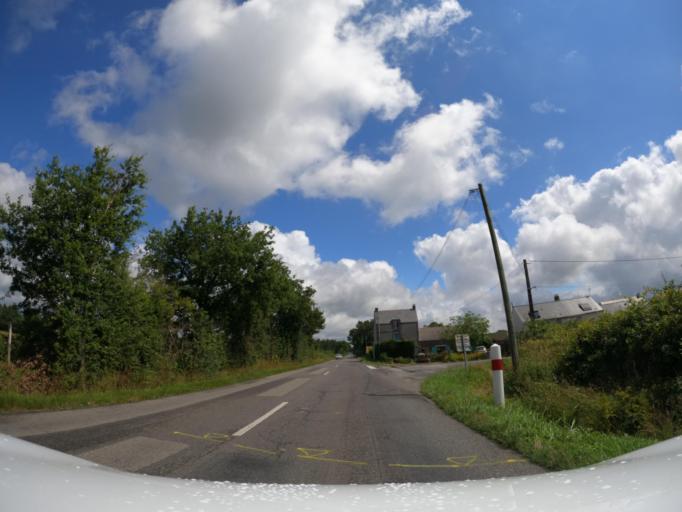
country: FR
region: Pays de la Loire
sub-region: Departement de la Loire-Atlantique
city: Saint-Mars-du-Desert
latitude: 47.3829
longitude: -1.3923
